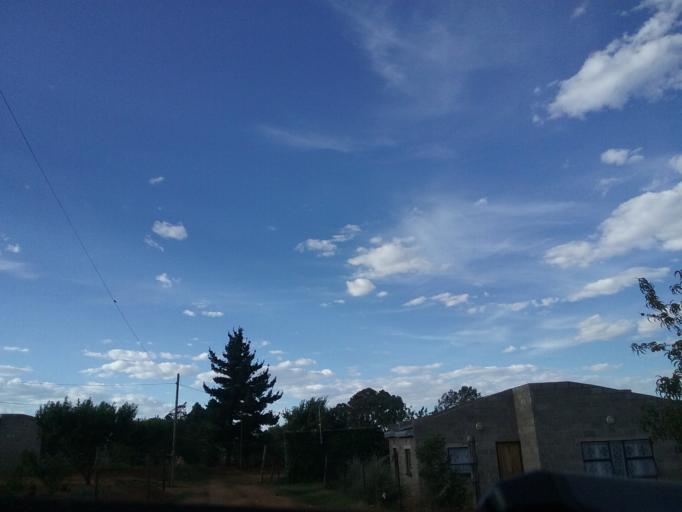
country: LS
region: Maseru
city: Maseru
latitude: -29.4267
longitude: 27.5734
